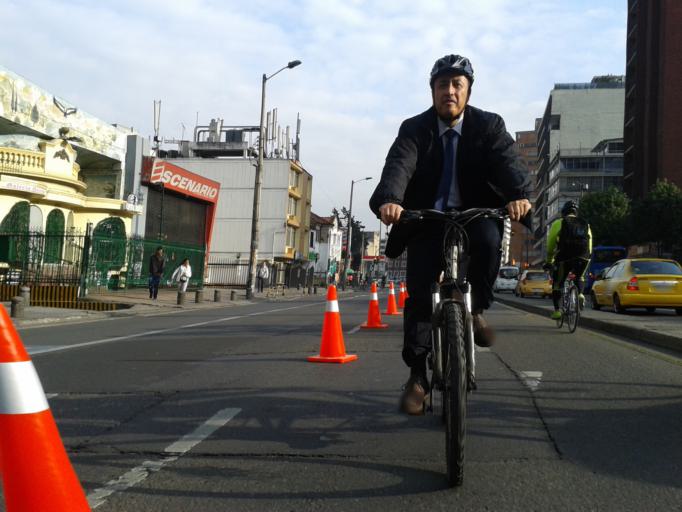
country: CO
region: Bogota D.C.
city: Bogota
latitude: 4.6429
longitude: -74.0618
